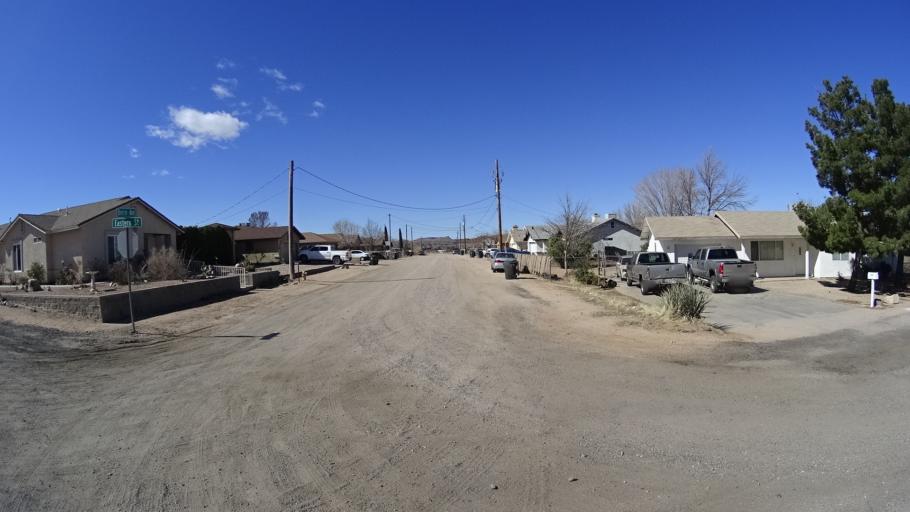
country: US
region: Arizona
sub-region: Mohave County
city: Kingman
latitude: 35.2071
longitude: -114.0115
